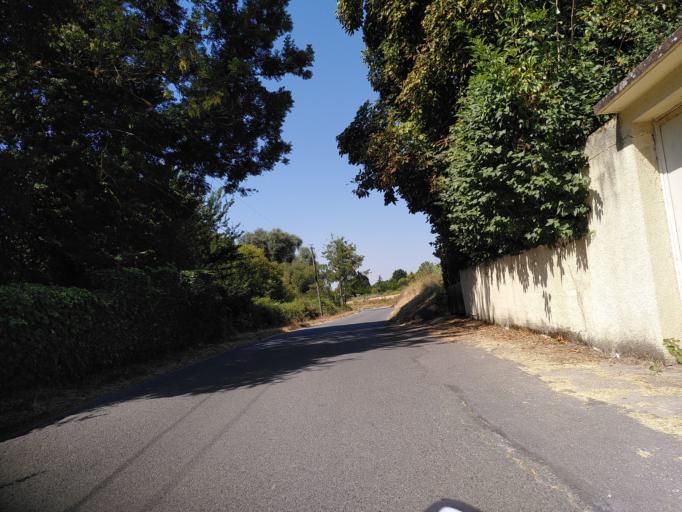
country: FR
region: Ile-de-France
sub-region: Departement de l'Essonne
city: Ollainville
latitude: 48.5856
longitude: 2.2141
